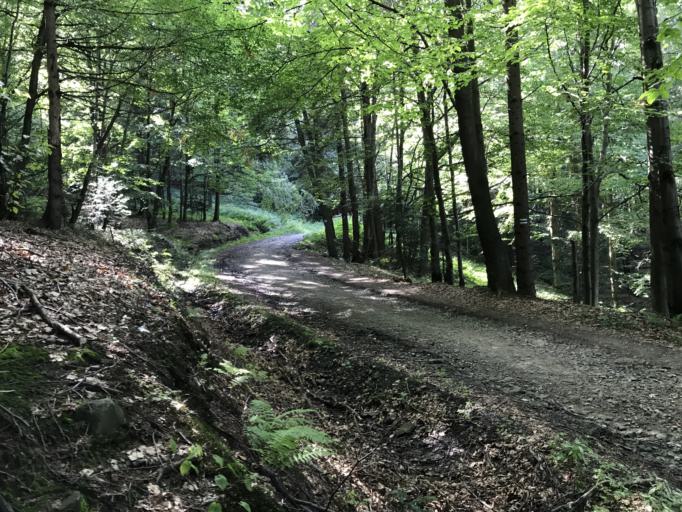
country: PL
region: Lesser Poland Voivodeship
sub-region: Powiat nowosadecki
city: Krynica-Zdroj
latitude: 49.4218
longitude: 20.9151
